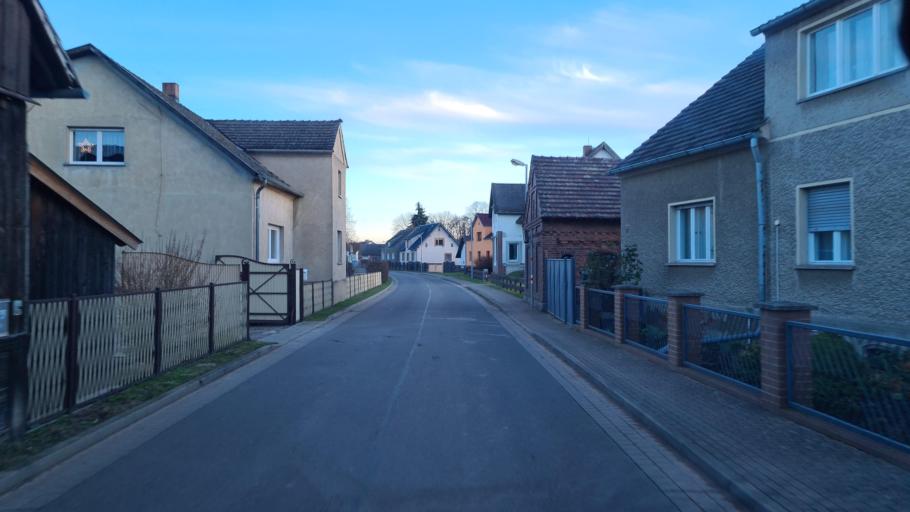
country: DE
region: Brandenburg
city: Burg
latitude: 51.8134
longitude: 14.1334
